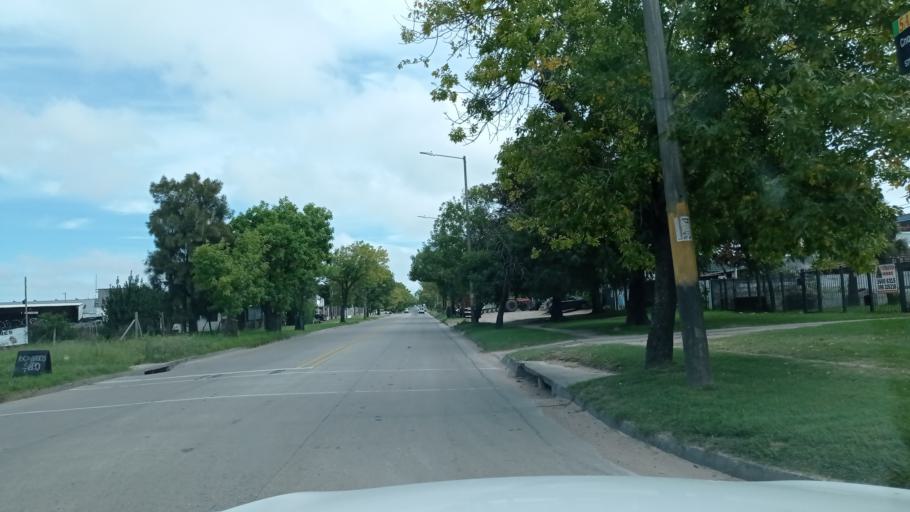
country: UY
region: Canelones
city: Paso de Carrasco
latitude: -34.8712
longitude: -56.0878
